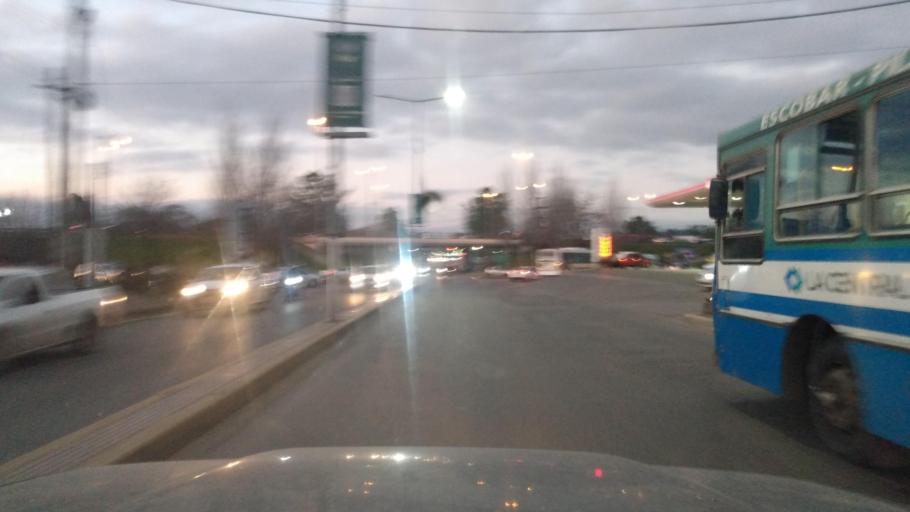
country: AR
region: Buenos Aires
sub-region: Partido de Pilar
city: Pilar
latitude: -34.4506
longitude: -58.9064
